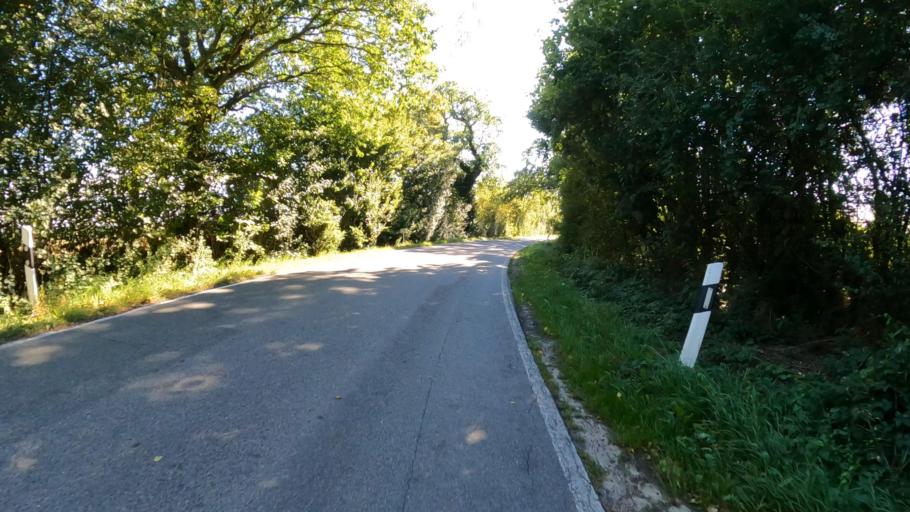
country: DE
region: Schleswig-Holstein
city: Westerau
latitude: 53.7744
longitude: 10.5200
